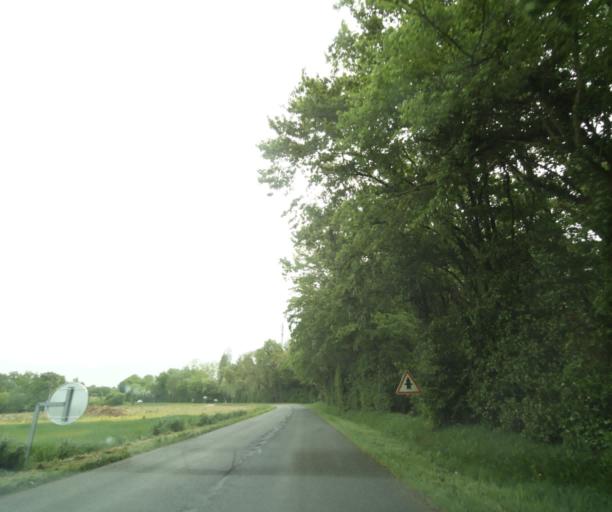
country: FR
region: Poitou-Charentes
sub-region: Departement de la Charente-Maritime
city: Chaniers
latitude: 45.7623
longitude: -0.5326
